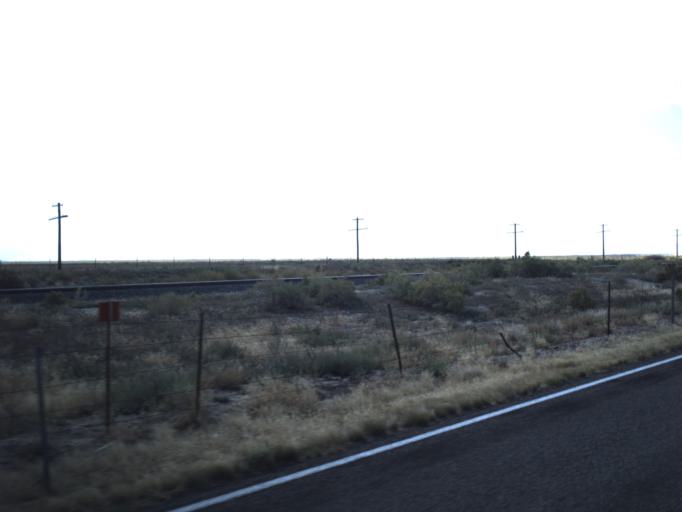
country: US
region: Utah
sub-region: Millard County
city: Delta
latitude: 39.0510
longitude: -112.7672
